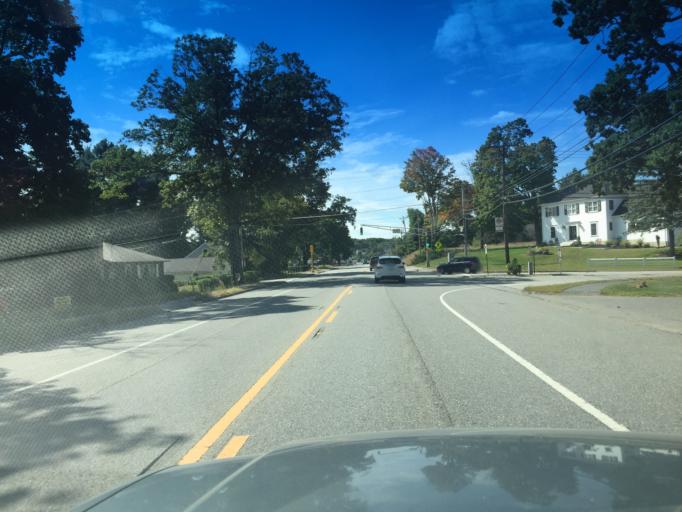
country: US
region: Massachusetts
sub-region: Worcester County
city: Northborough
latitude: 42.3121
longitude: -71.6541
